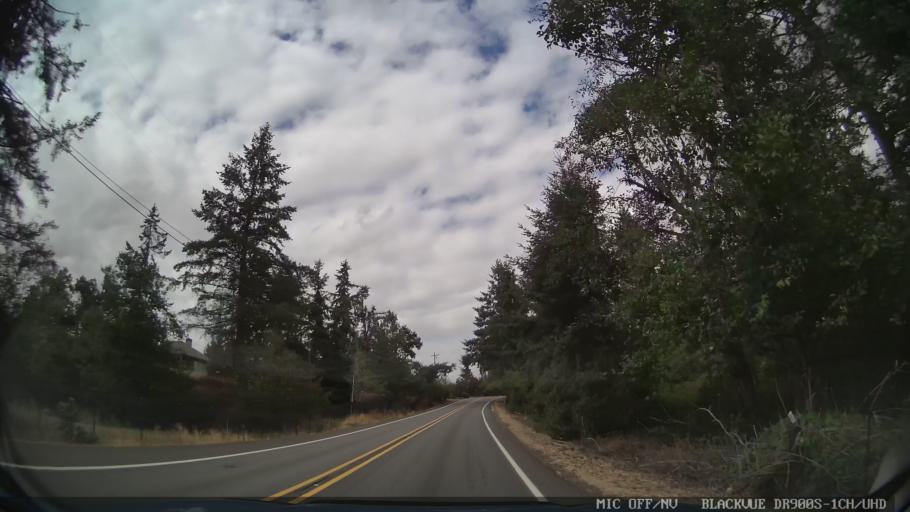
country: US
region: Oregon
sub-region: Marion County
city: Sublimity
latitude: 44.8486
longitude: -122.7945
